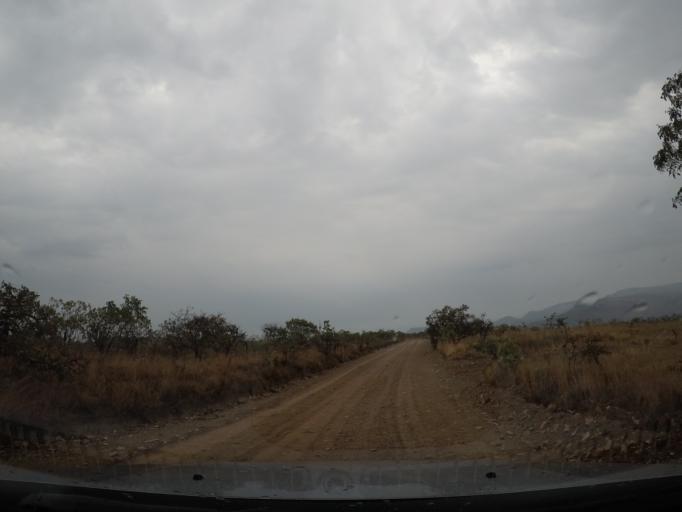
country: BR
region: Goias
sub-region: Pirenopolis
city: Pirenopolis
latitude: -15.8201
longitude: -48.9025
